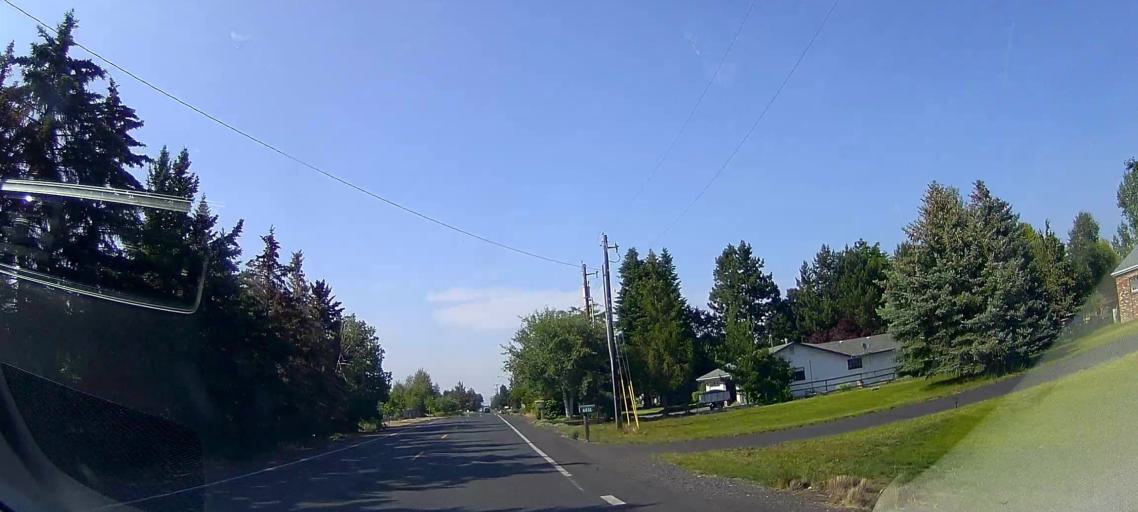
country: US
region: Oregon
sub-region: Deschutes County
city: Bend
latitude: 44.0451
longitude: -121.2686
